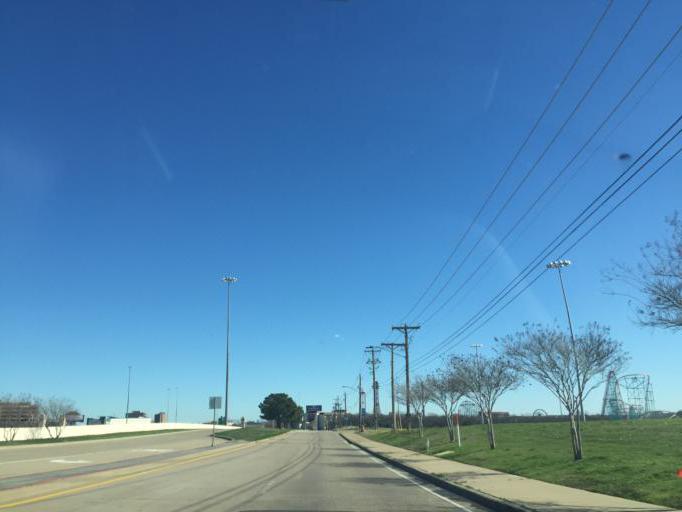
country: US
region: Texas
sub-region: Tarrant County
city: Arlington
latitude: 32.7591
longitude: -97.0834
